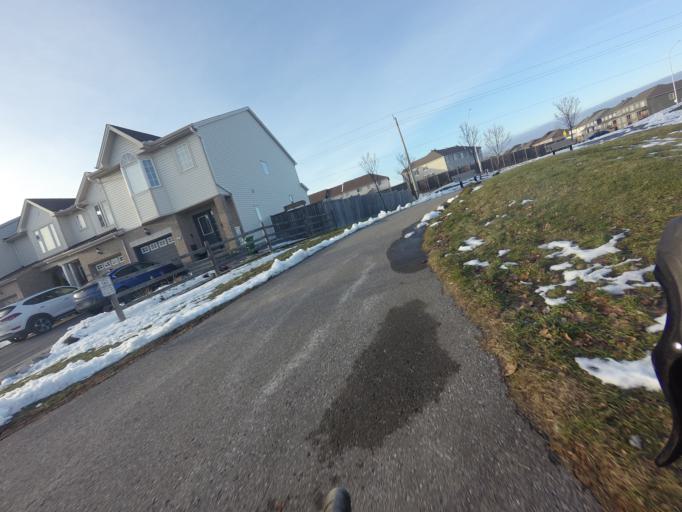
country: CA
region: Ontario
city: Bells Corners
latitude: 45.2765
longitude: -75.8647
